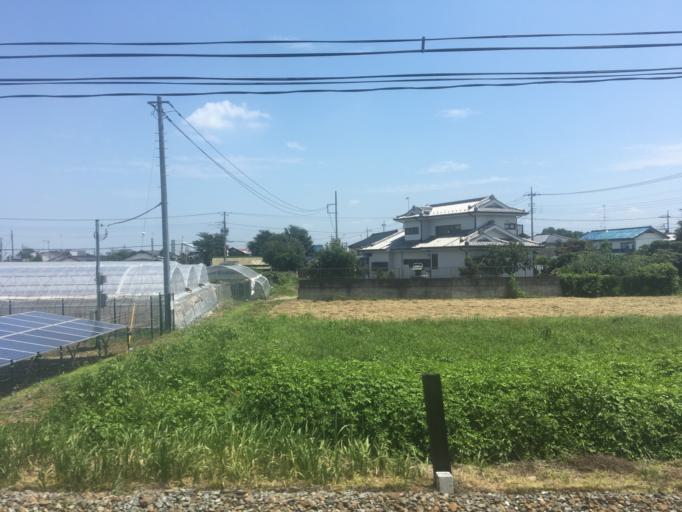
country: JP
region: Saitama
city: Yorii
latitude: 36.1233
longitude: 139.2011
